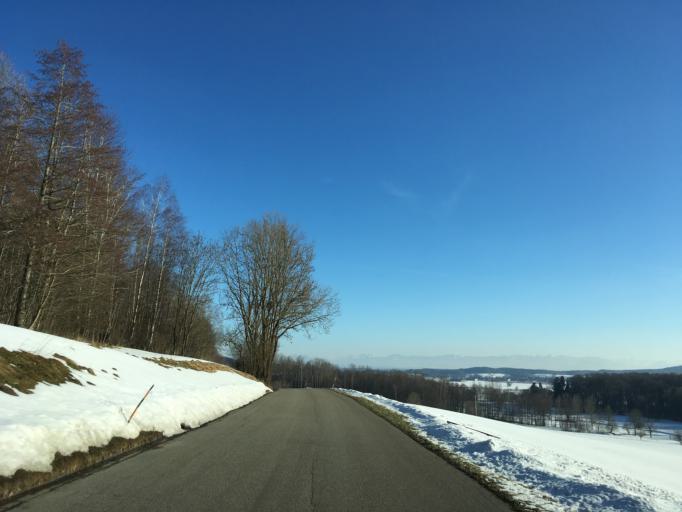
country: DE
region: Bavaria
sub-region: Upper Bavaria
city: Steinhoring
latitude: 48.1127
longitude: 12.0187
